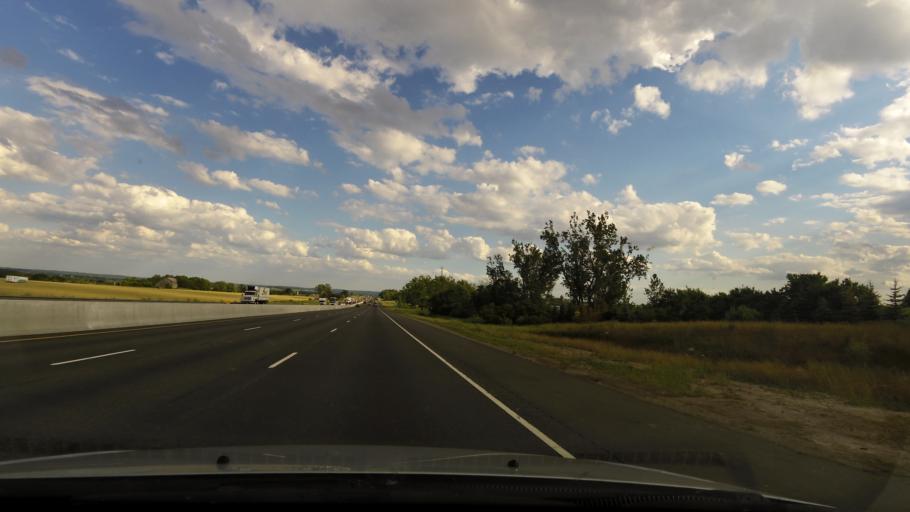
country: CA
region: Ontario
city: Bradford West Gwillimbury
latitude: 44.1189
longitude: -79.6357
